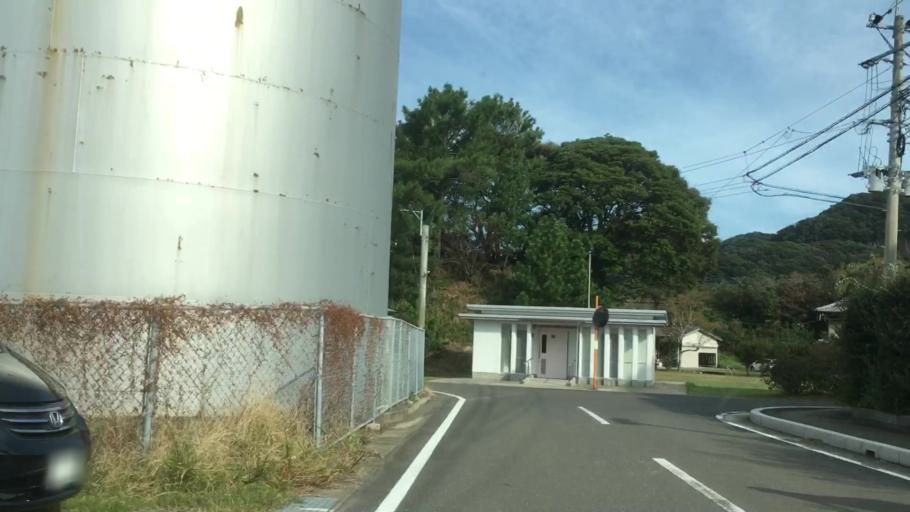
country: JP
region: Nagasaki
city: Sasebo
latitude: 32.9443
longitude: 129.6376
